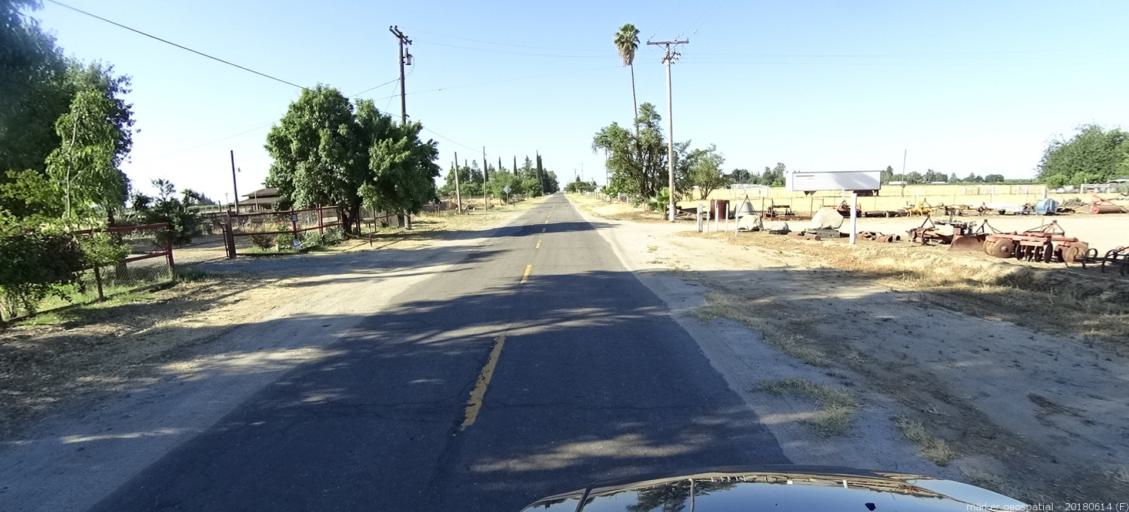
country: US
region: California
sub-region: Madera County
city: Madera
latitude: 36.9587
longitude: -120.1194
